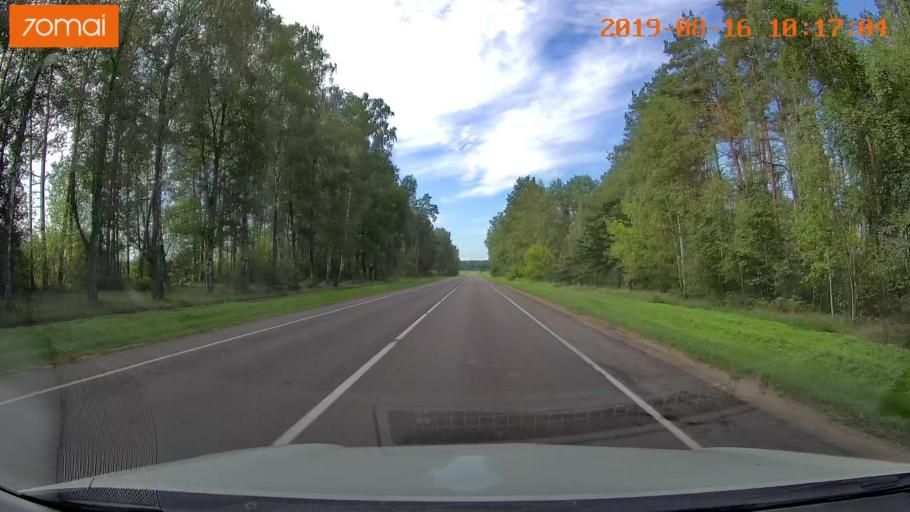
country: BY
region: Mogilev
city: Asipovichy
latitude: 53.3154
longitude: 28.7160
